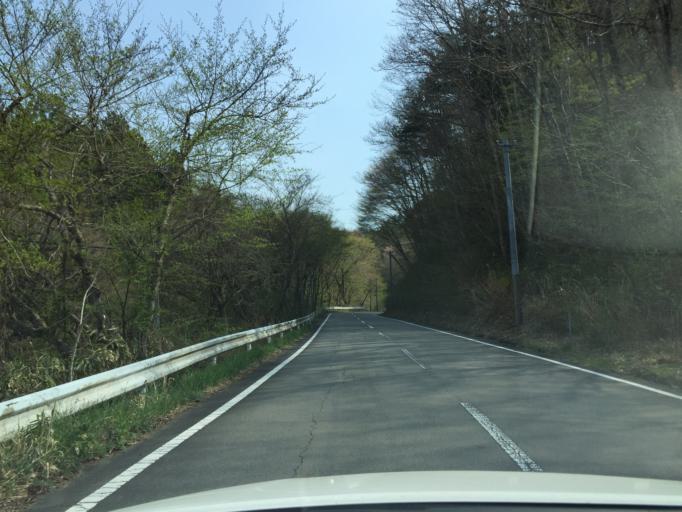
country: JP
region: Fukushima
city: Iwaki
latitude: 37.2387
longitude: 140.8460
